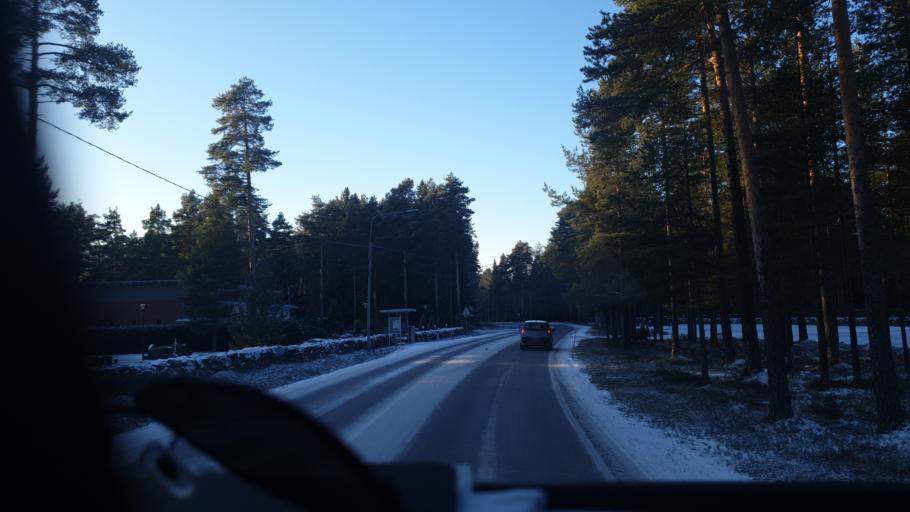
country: FI
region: Central Ostrobothnia
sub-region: Kokkola
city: Kokkola
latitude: 63.8272
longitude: 23.0983
